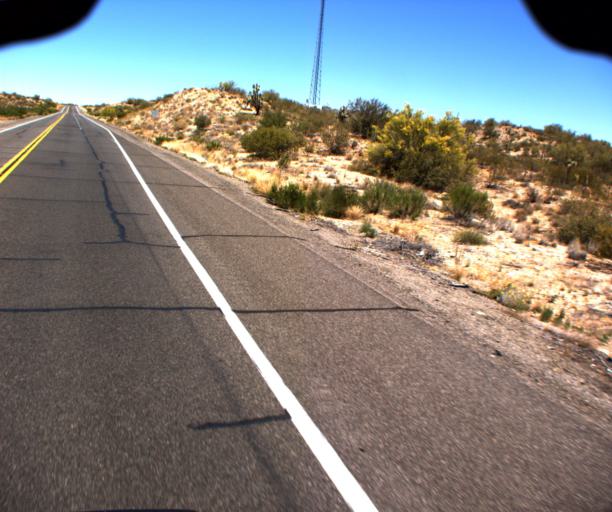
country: US
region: Arizona
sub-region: Yavapai County
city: Congress
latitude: 34.2135
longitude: -113.0665
